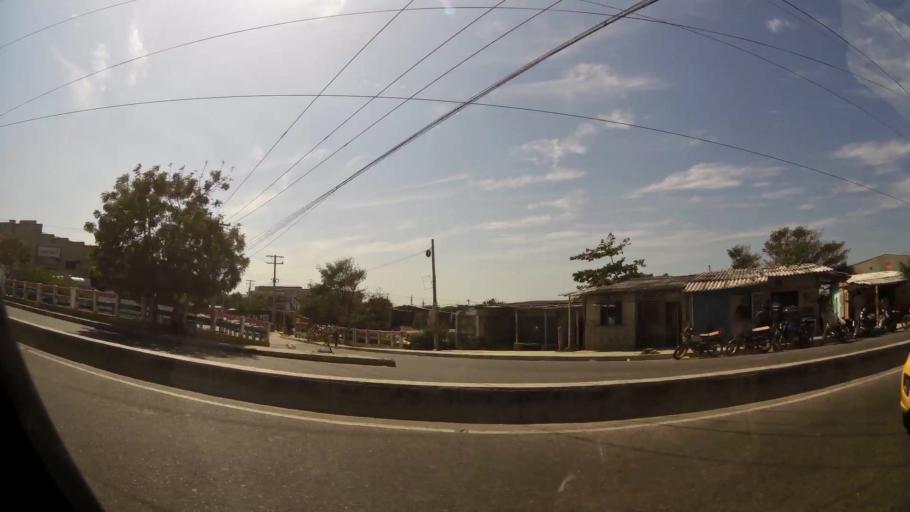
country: CO
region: Atlantico
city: Barranquilla
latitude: 10.9643
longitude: -74.8385
